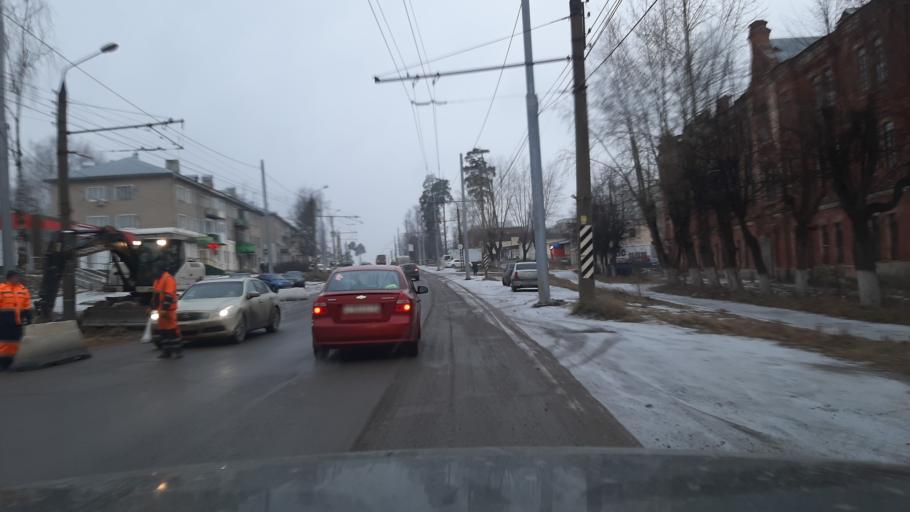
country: RU
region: Ivanovo
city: Kokhma
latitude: 56.9334
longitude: 41.0761
